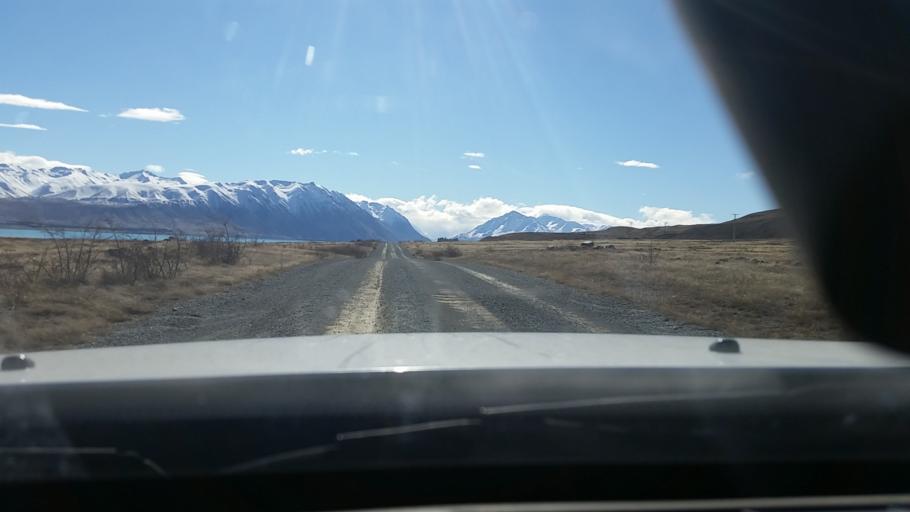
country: NZ
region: Canterbury
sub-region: Timaru District
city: Pleasant Point
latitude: -43.9181
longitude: 170.5586
